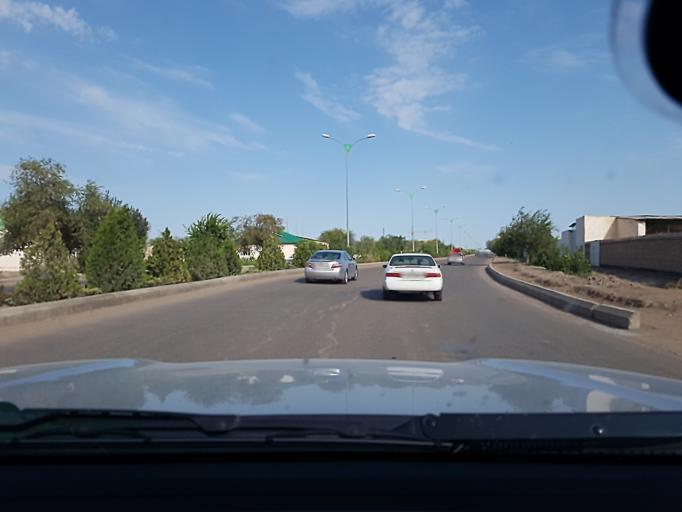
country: TM
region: Dasoguz
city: Koeneuergench
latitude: 42.3200
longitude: 59.1603
